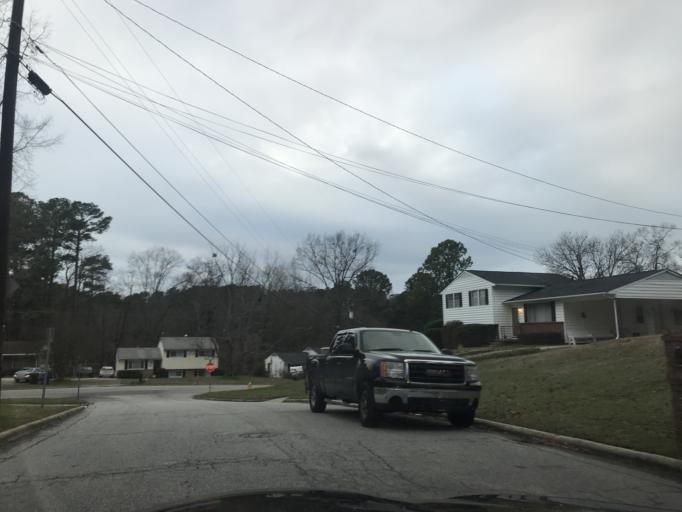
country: US
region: North Carolina
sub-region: Wake County
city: Raleigh
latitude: 35.7509
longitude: -78.6091
